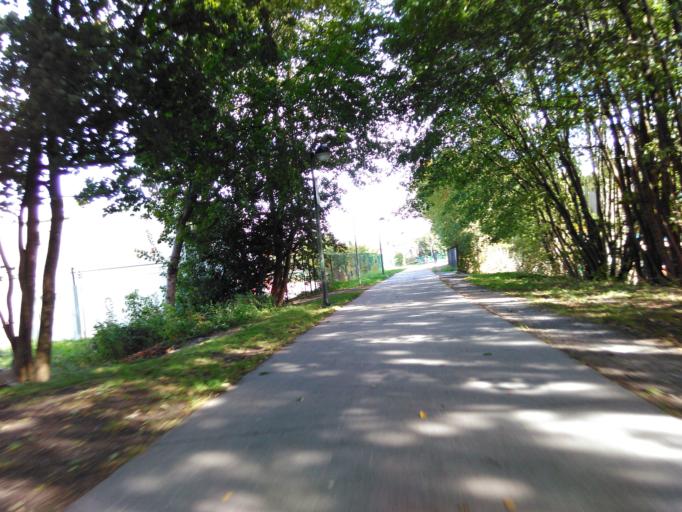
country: BE
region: Wallonia
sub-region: Province du Luxembourg
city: Bastogne
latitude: 50.0040
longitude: 5.7154
